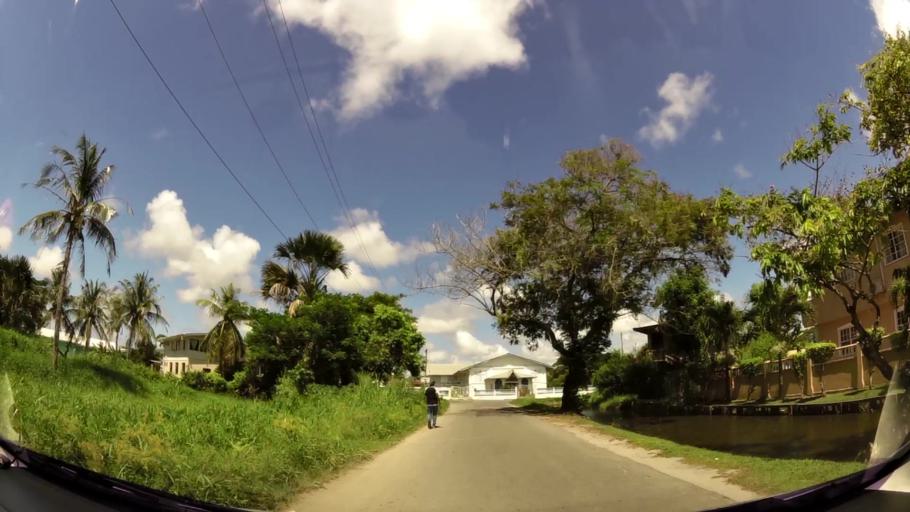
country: GY
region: Demerara-Mahaica
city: Georgetown
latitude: 6.7992
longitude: -58.1383
